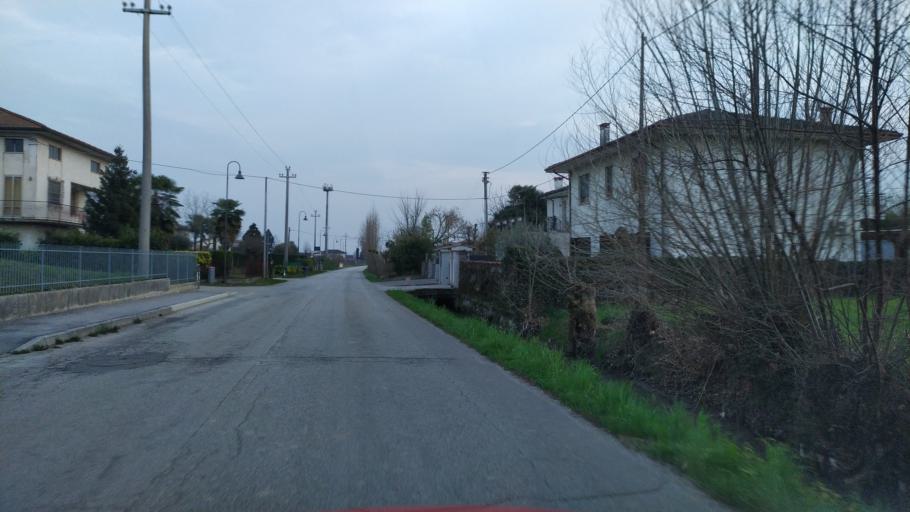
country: IT
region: Veneto
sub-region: Provincia di Vicenza
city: Vigardolo
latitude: 45.6242
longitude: 11.5772
